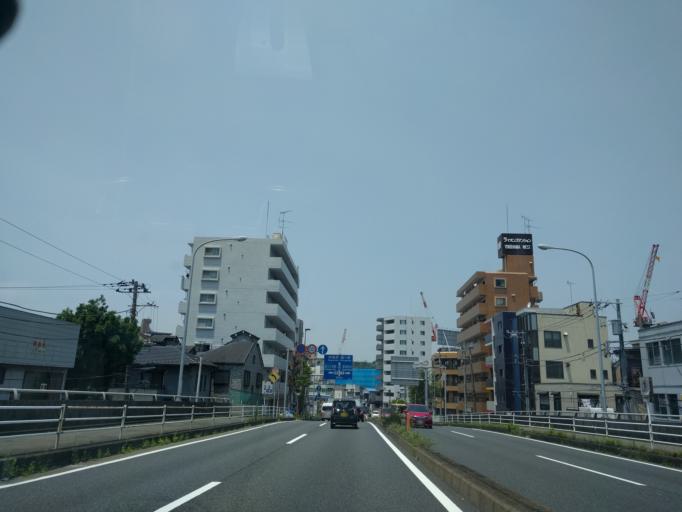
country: JP
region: Kanagawa
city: Yokohama
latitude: 35.4550
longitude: 139.6087
